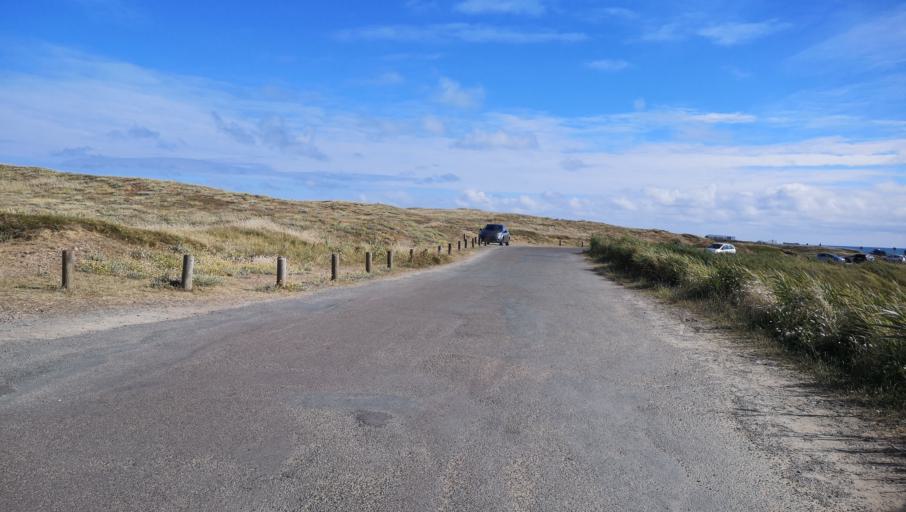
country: FR
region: Pays de la Loire
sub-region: Departement de la Vendee
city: Les Sables-d'Olonne
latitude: 46.5120
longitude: -1.8175
